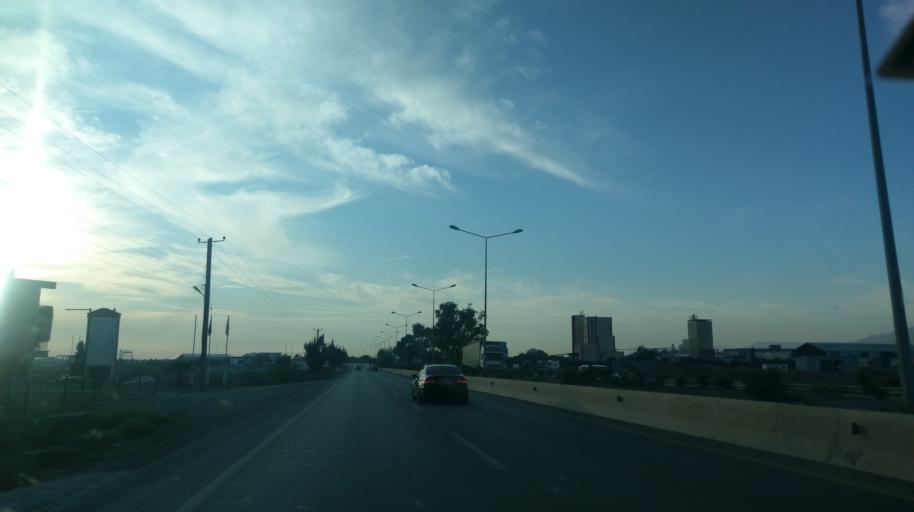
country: CY
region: Lefkosia
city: Nicosia
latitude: 35.2184
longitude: 33.4631
